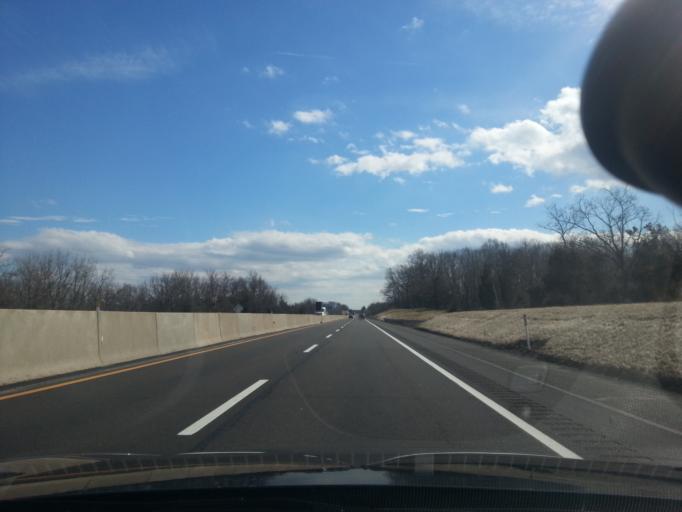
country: US
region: Pennsylvania
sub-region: Montgomery County
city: Harleysville
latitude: 40.3156
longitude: -75.3756
